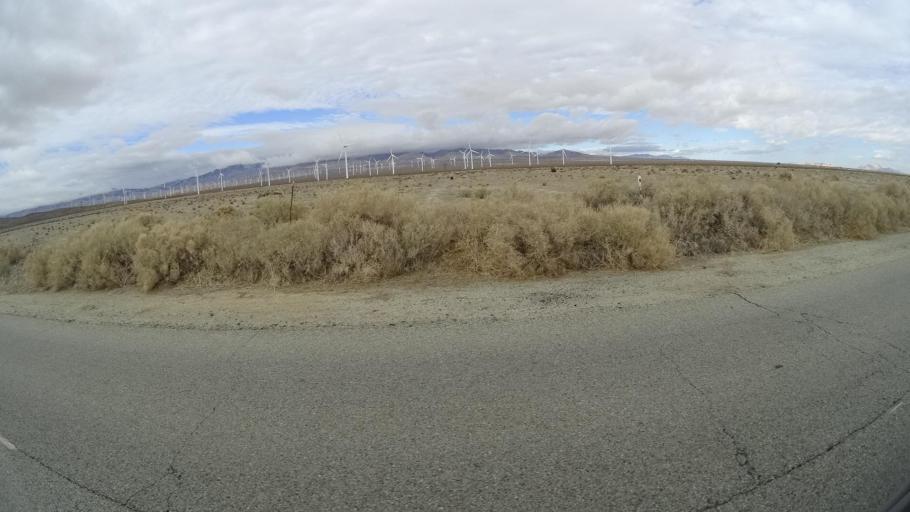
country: US
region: California
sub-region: Los Angeles County
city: Green Valley
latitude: 34.8626
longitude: -118.4127
